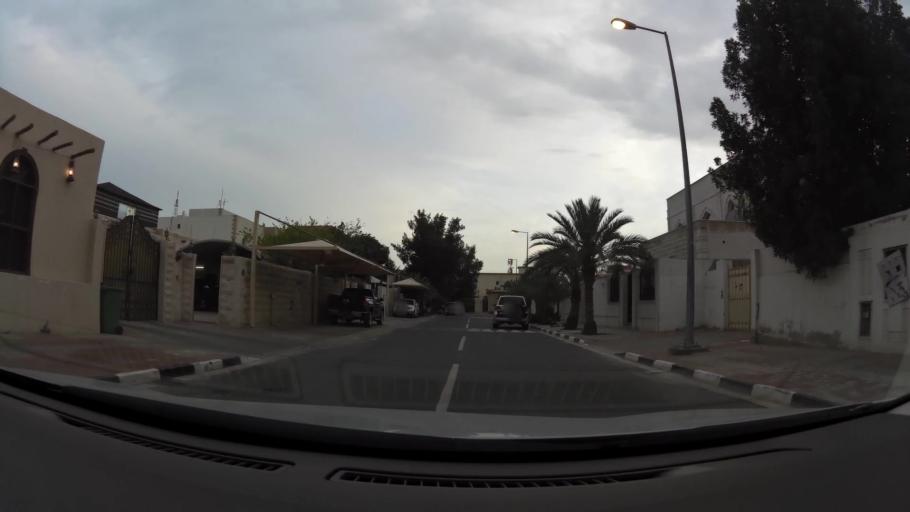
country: QA
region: Baladiyat ad Dawhah
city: Doha
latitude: 25.3396
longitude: 51.5101
